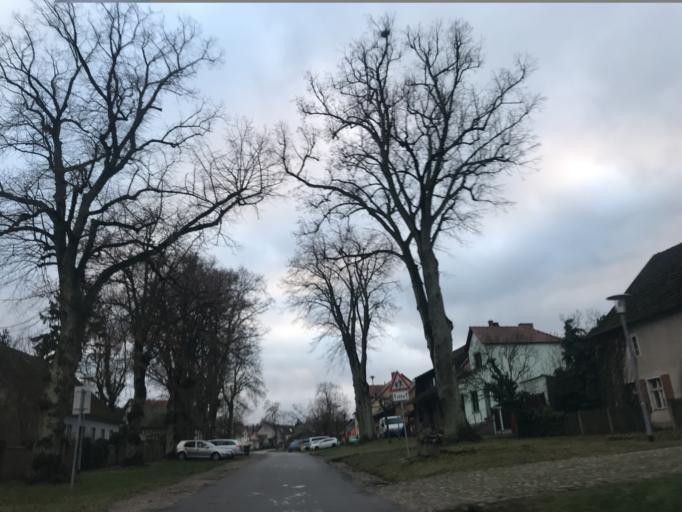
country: DE
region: Brandenburg
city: Rheinsberg
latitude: 53.0988
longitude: 12.8302
